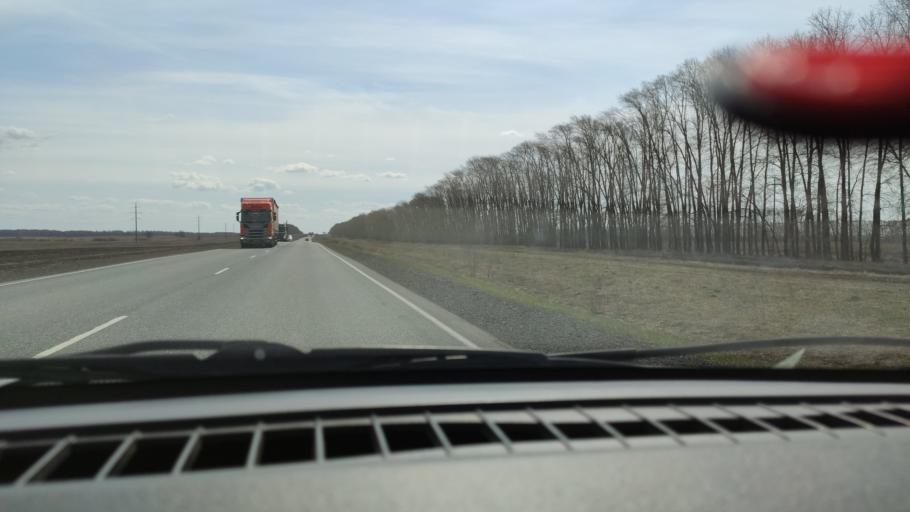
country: RU
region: Bashkortostan
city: Kushnarenkovo
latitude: 55.2418
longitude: 55.0763
